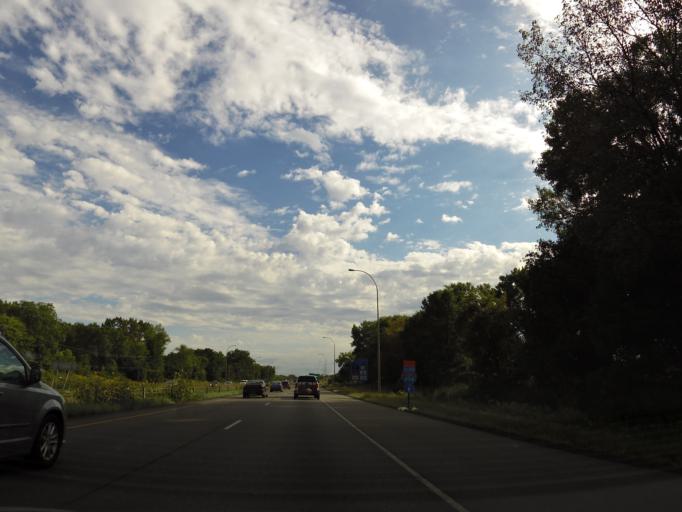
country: US
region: Minnesota
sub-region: Hennepin County
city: New Hope
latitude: 45.0659
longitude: -93.4010
